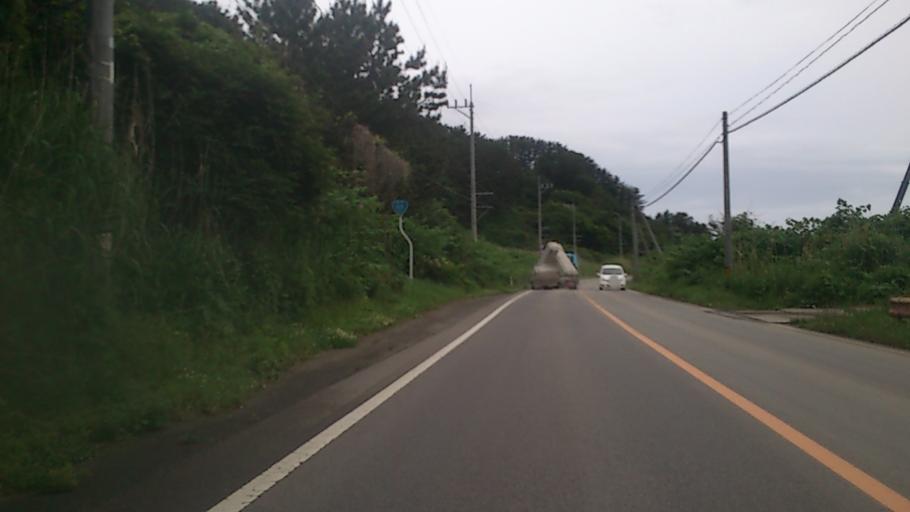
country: JP
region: Akita
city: Noshiromachi
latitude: 40.5087
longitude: 139.9507
